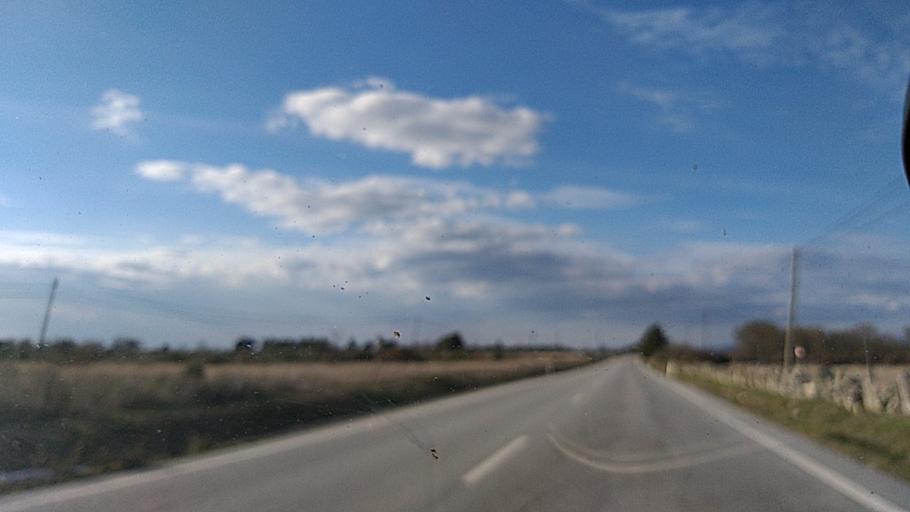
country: ES
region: Castille and Leon
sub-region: Provincia de Salamanca
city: Fuentes de Onoro
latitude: 40.6277
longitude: -6.8503
